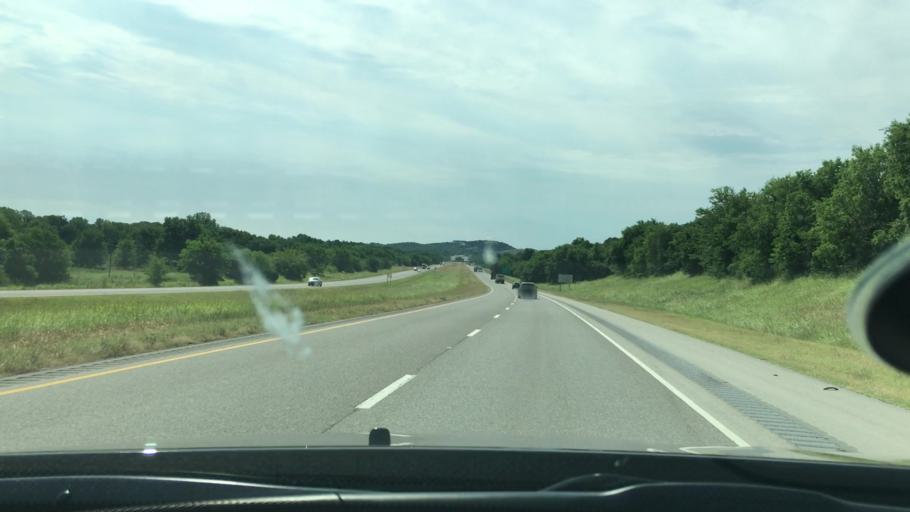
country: US
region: Oklahoma
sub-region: Murray County
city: Davis
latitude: 34.4685
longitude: -97.1526
